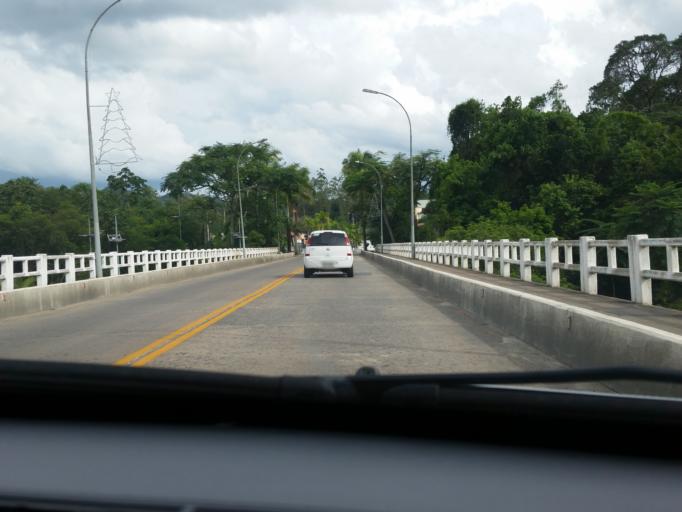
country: BR
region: Santa Catarina
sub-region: Indaial
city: Indaial
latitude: -26.8957
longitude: -49.2381
